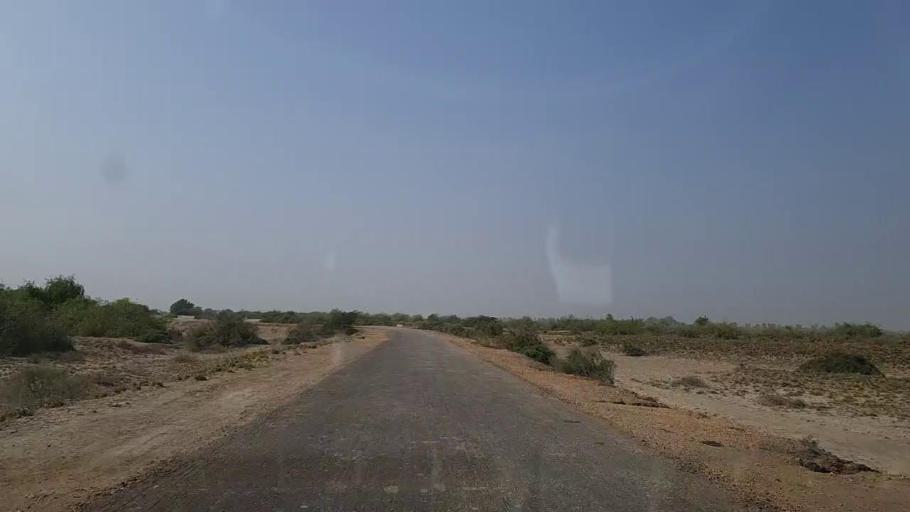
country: PK
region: Sindh
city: Mirpur Sakro
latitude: 24.5296
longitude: 67.5594
